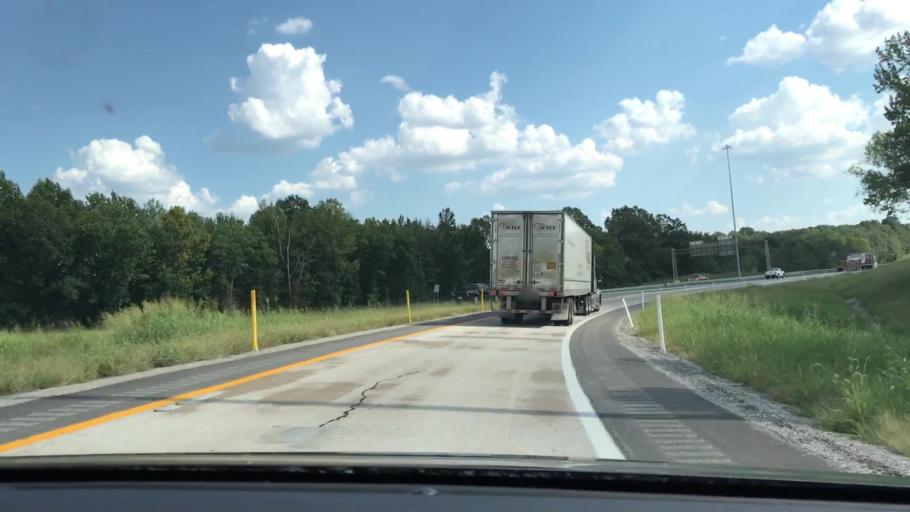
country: US
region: Kentucky
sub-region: Ohio County
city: Oak Grove
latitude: 37.3815
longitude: -86.8079
